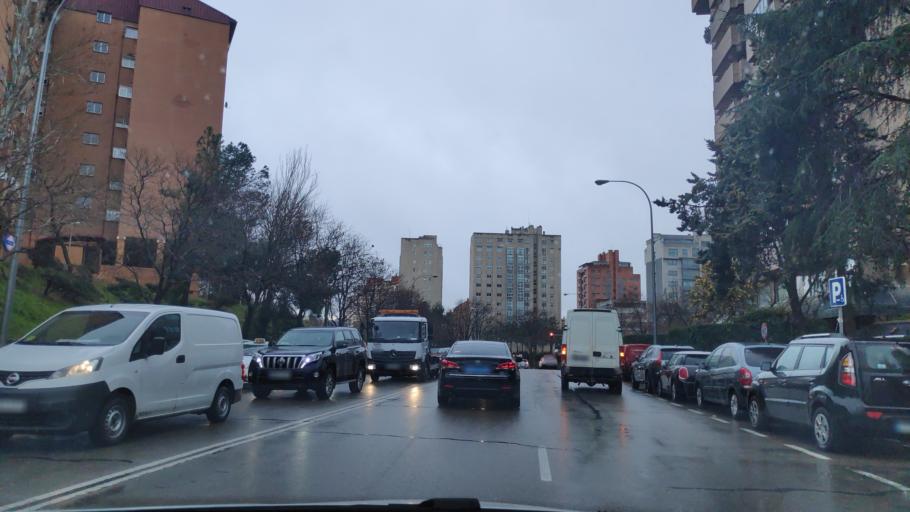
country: ES
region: Madrid
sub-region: Provincia de Madrid
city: Ciudad Lineal
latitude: 40.4532
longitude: -3.6606
